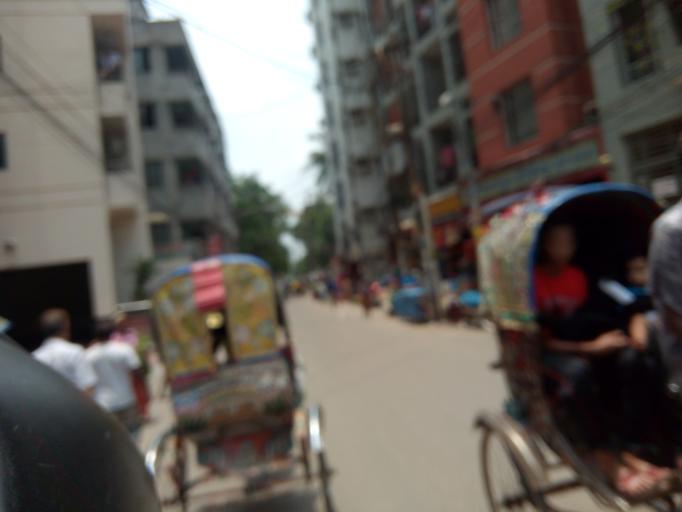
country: BD
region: Dhaka
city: Paltan
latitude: 23.7511
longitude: 90.4094
